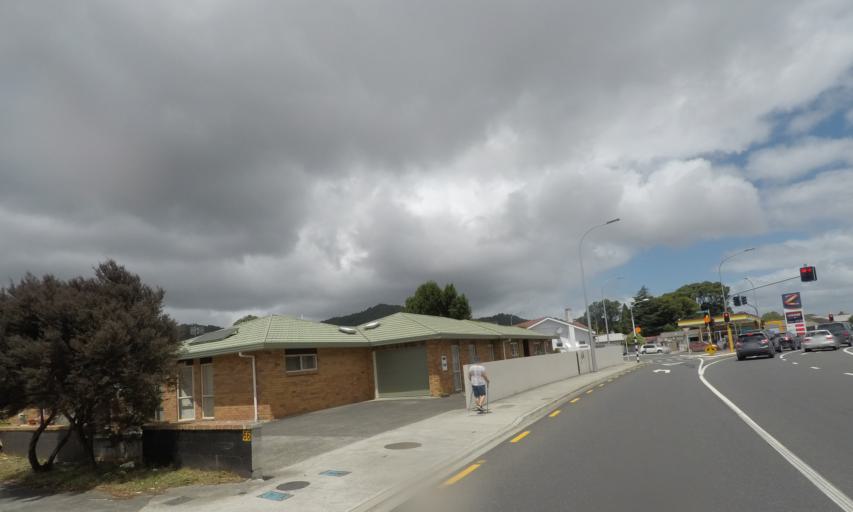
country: NZ
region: Northland
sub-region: Whangarei
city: Whangarei
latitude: -35.7078
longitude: 174.3214
